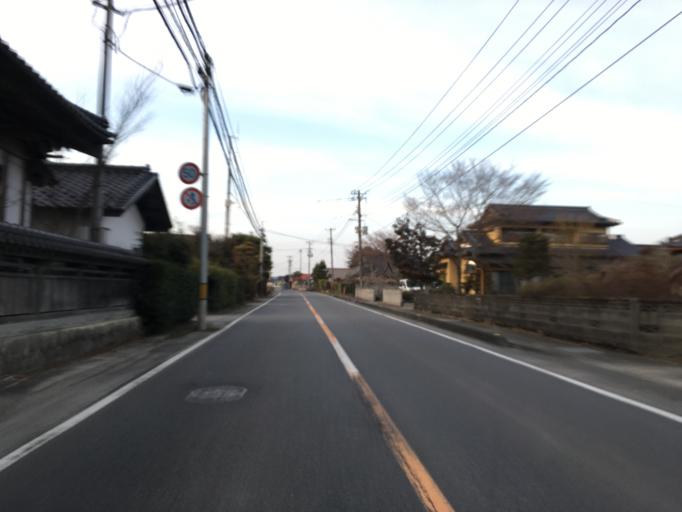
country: JP
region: Ibaraki
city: Daigo
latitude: 36.9320
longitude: 140.4087
